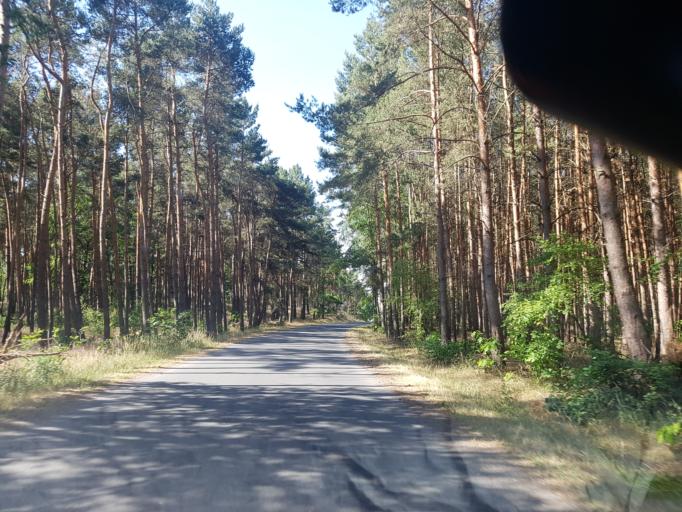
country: DE
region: Brandenburg
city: Treuenbrietzen
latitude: 52.0451
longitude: 12.8697
